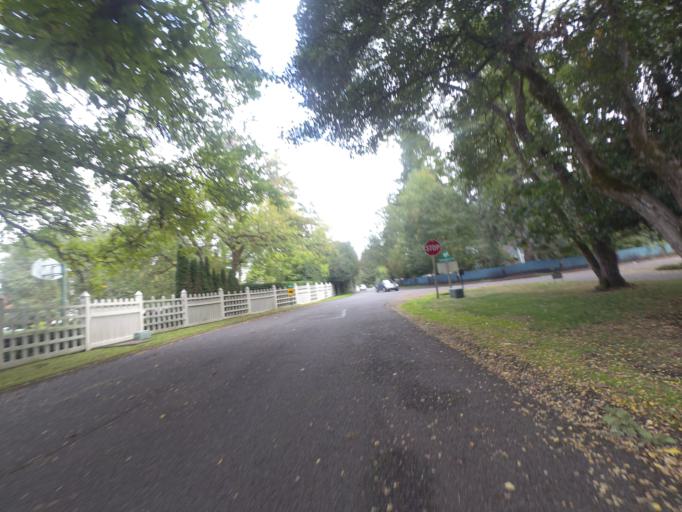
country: US
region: Washington
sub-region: Pierce County
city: Lakewood
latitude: 47.1701
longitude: -122.5325
